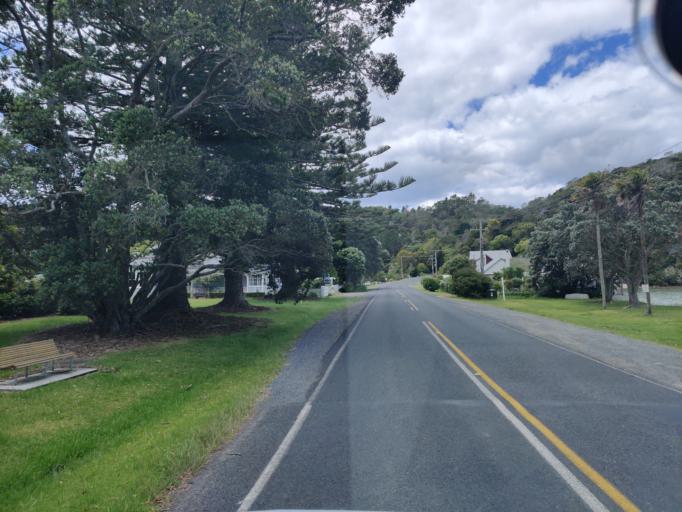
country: NZ
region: Northland
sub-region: Far North District
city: Paihia
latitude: -35.2659
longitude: 174.1274
